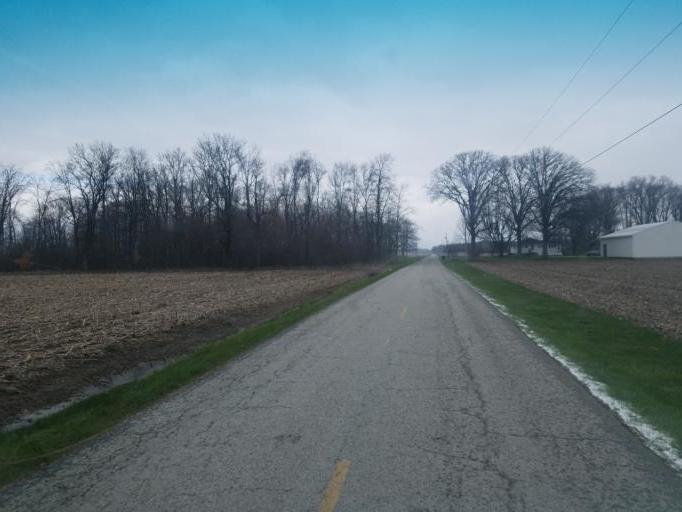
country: US
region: Ohio
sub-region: Marion County
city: Prospect
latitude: 40.4101
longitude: -83.1162
